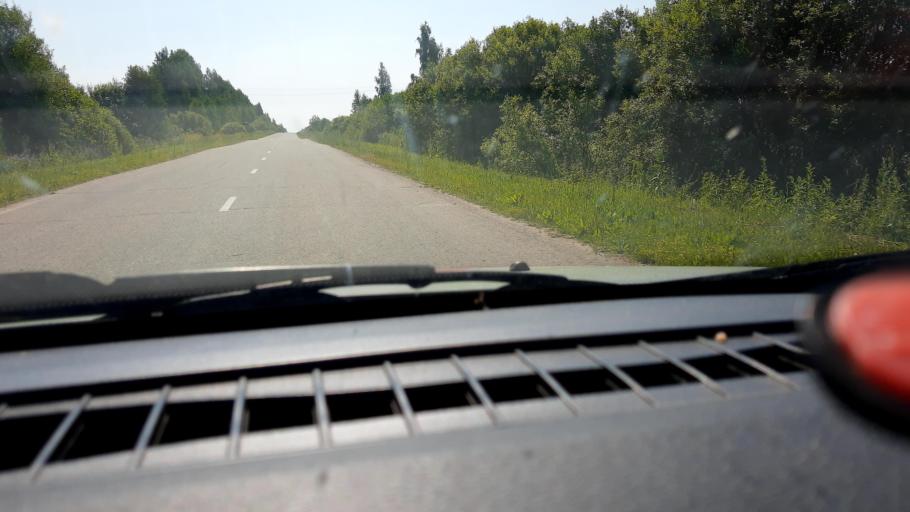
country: RU
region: Nizjnij Novgorod
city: Sharanga
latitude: 57.0448
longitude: 46.5535
